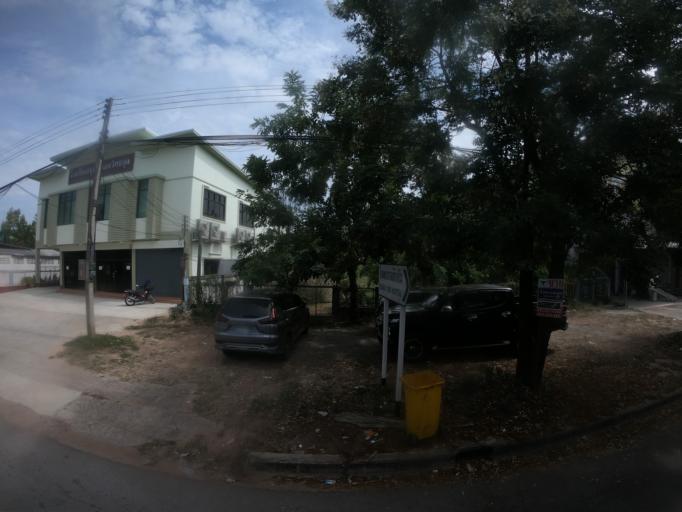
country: TH
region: Maha Sarakham
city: Chiang Yuen
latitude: 16.4040
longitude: 103.0992
